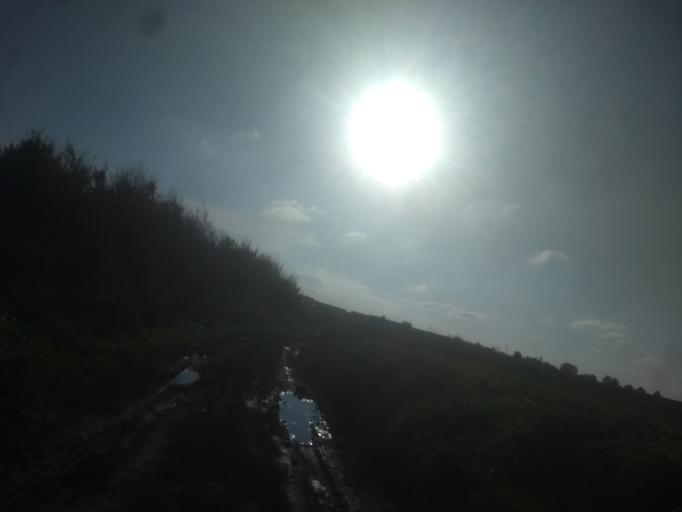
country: FR
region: Nord-Pas-de-Calais
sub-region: Departement du Pas-de-Calais
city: Tilloy-les-Mofflaines
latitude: 50.2761
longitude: 2.8027
